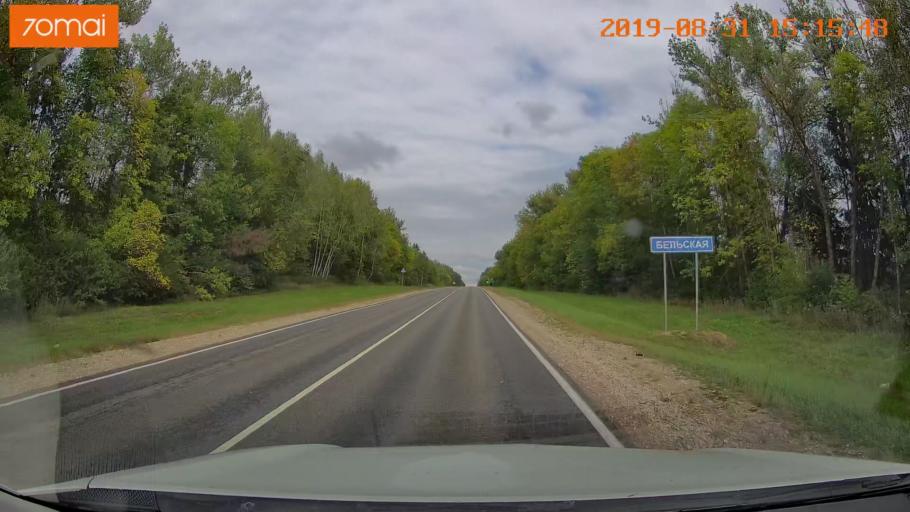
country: RU
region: Kaluga
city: Baryatino
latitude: 54.4545
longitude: 34.3350
